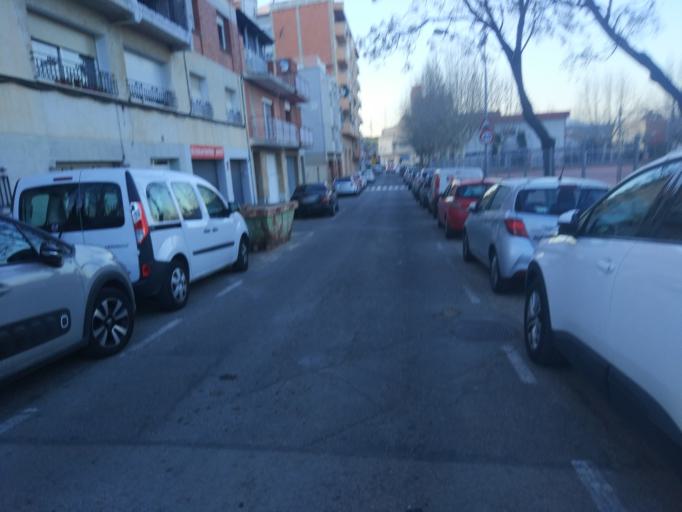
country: ES
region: Catalonia
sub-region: Provincia de Barcelona
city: Rubi
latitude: 41.4893
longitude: 2.0260
